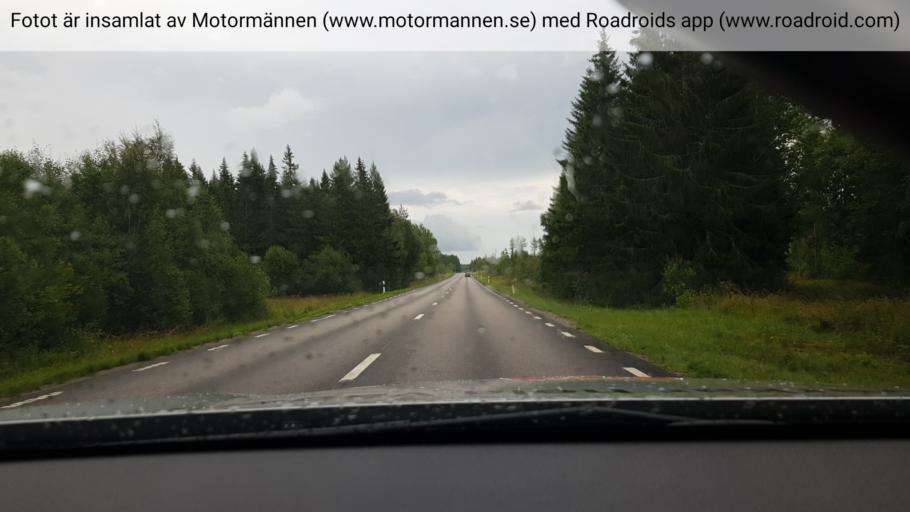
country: SE
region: Uppsala
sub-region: Tierps Kommun
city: Karlholmsbruk
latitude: 60.5408
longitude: 17.5545
